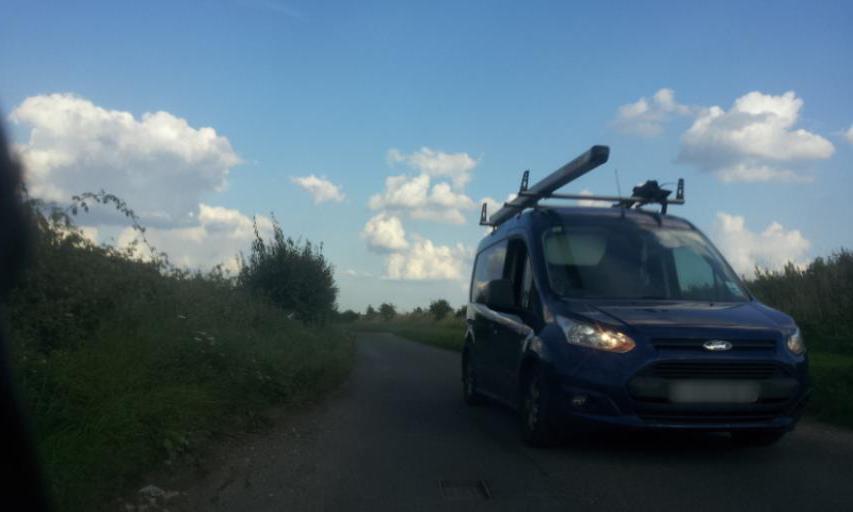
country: GB
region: England
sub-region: Kent
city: Eynsford
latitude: 51.4043
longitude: 0.2144
